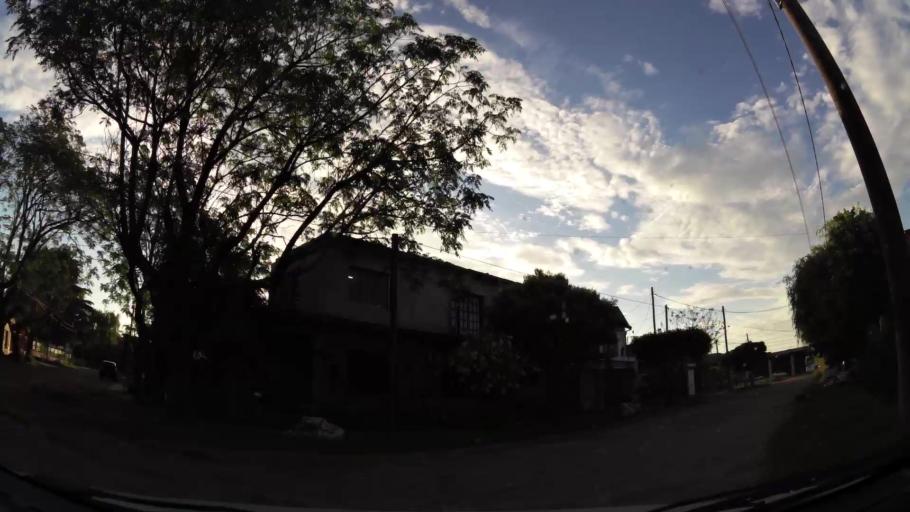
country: AR
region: Buenos Aires
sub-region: Partido de Merlo
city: Merlo
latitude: -34.6767
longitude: -58.7535
